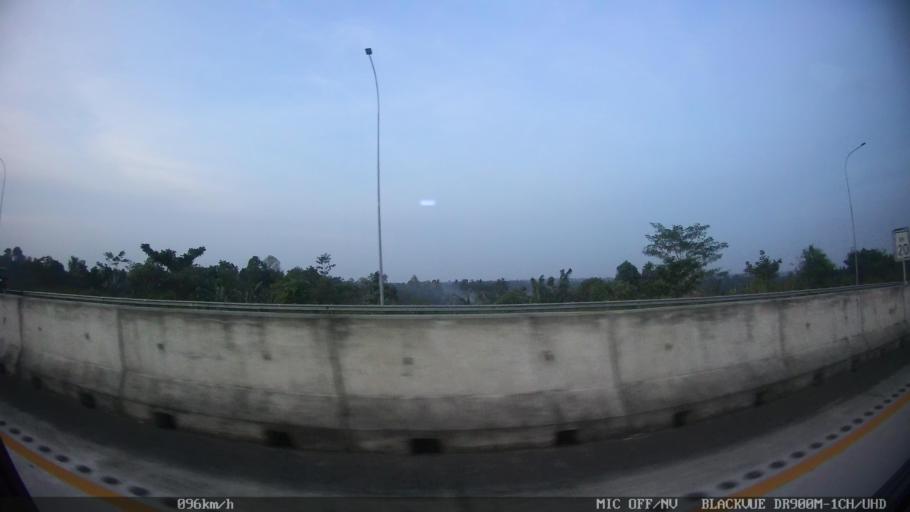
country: ID
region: Lampung
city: Pasuruan
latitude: -5.7300
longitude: 105.6738
